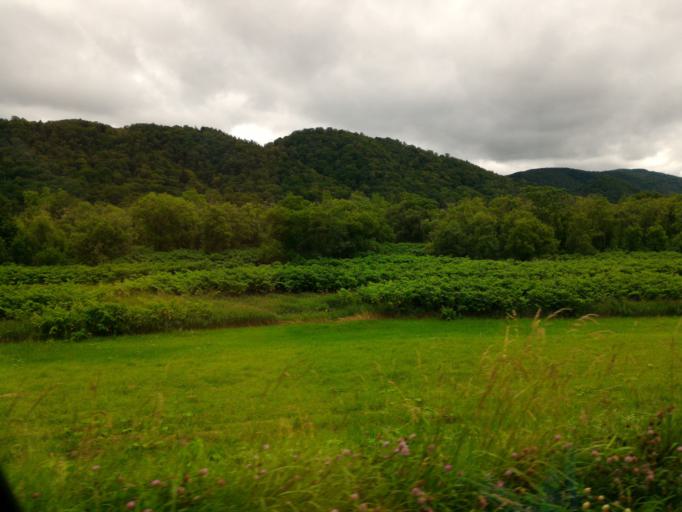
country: JP
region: Hokkaido
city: Nayoro
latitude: 44.7901
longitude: 142.0646
